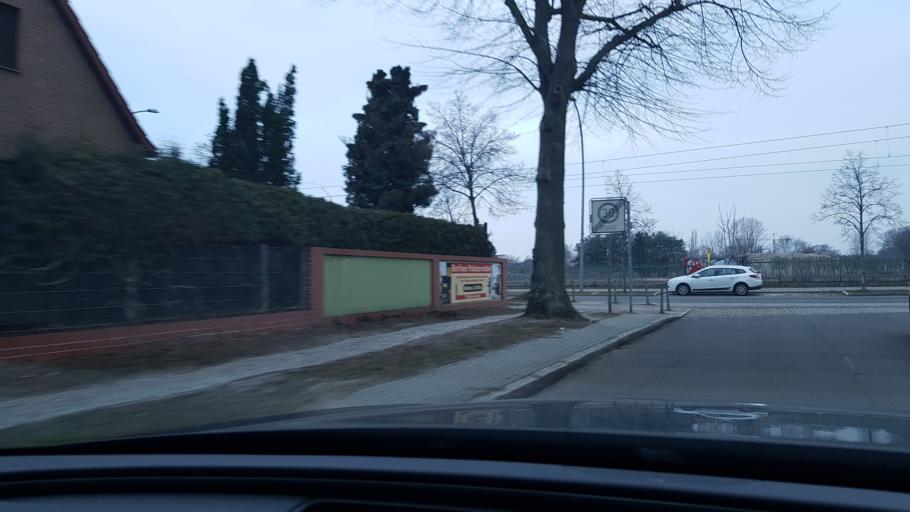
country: DE
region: Berlin
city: Berlin Koepenick
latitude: 52.4312
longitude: 13.5843
